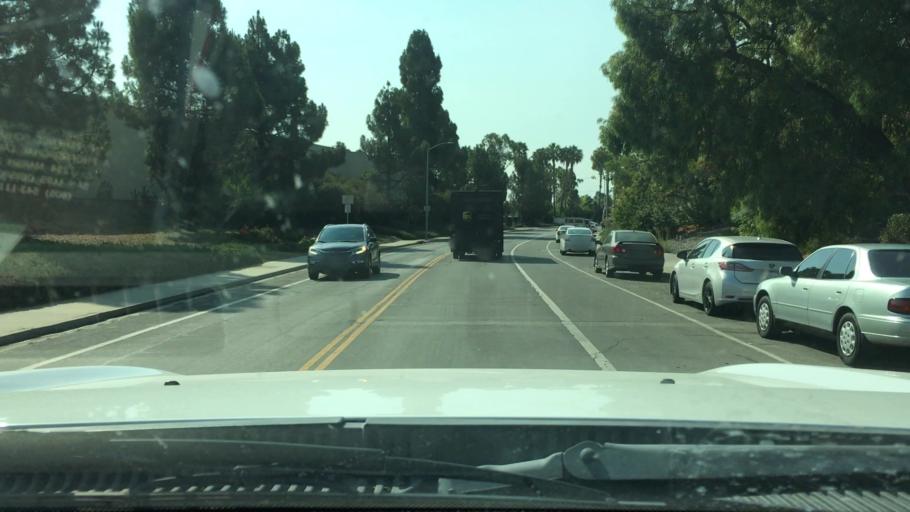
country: US
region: California
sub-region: San Luis Obispo County
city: San Luis Obispo
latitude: 35.2548
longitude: -120.6415
